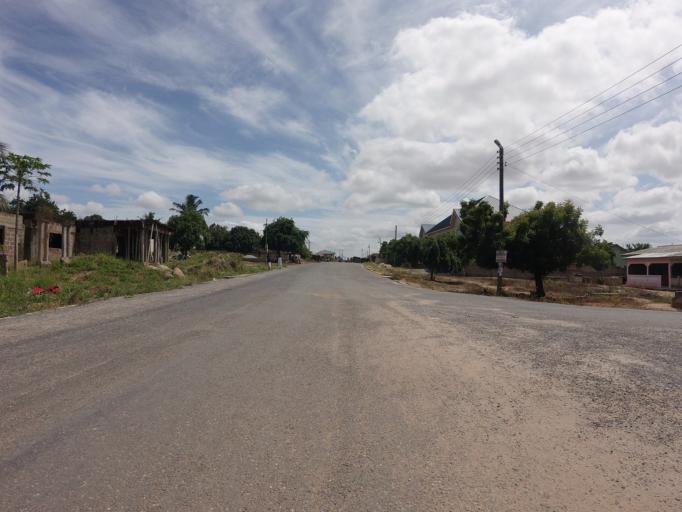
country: GH
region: Central
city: Kasoa
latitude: 5.5223
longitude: -0.4509
